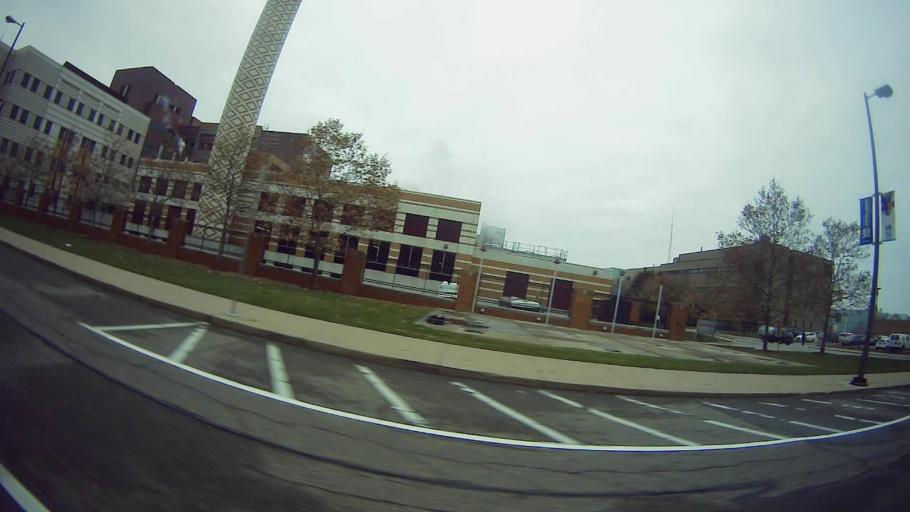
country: US
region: Michigan
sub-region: Wayne County
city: Detroit
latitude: 42.3573
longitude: -83.0589
